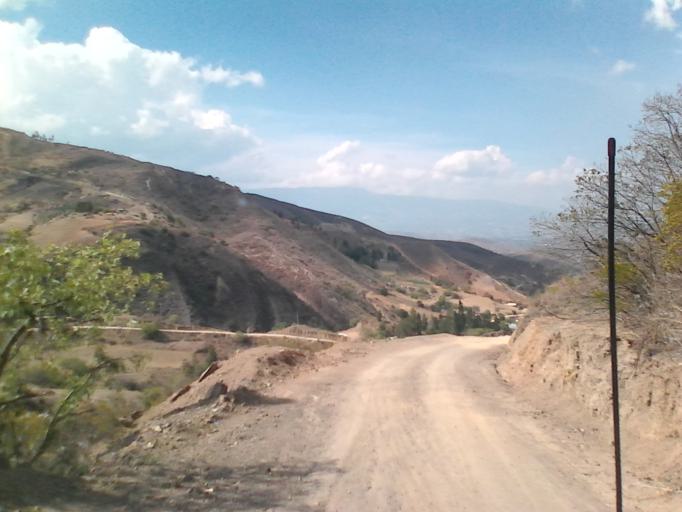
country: CO
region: Boyaca
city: Sachica
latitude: 5.5474
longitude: -73.5287
